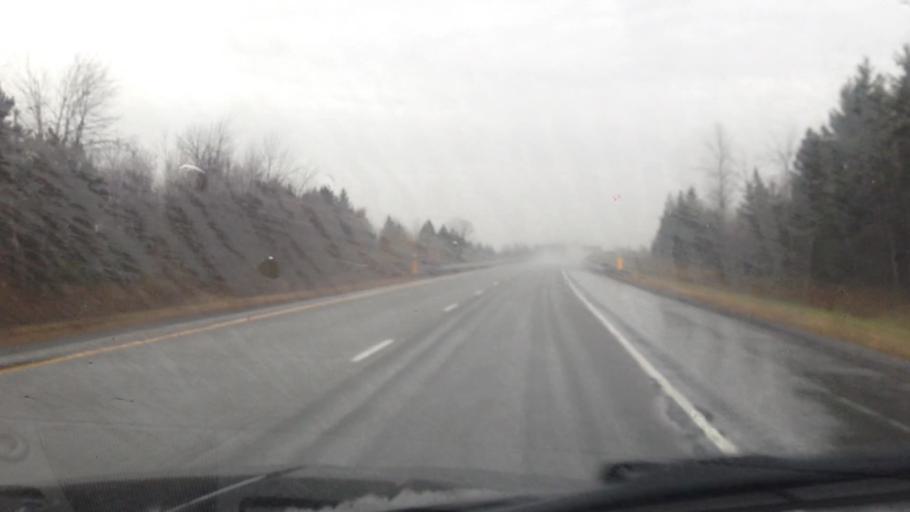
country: CA
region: Ontario
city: Casselman
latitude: 45.3046
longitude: -75.1092
